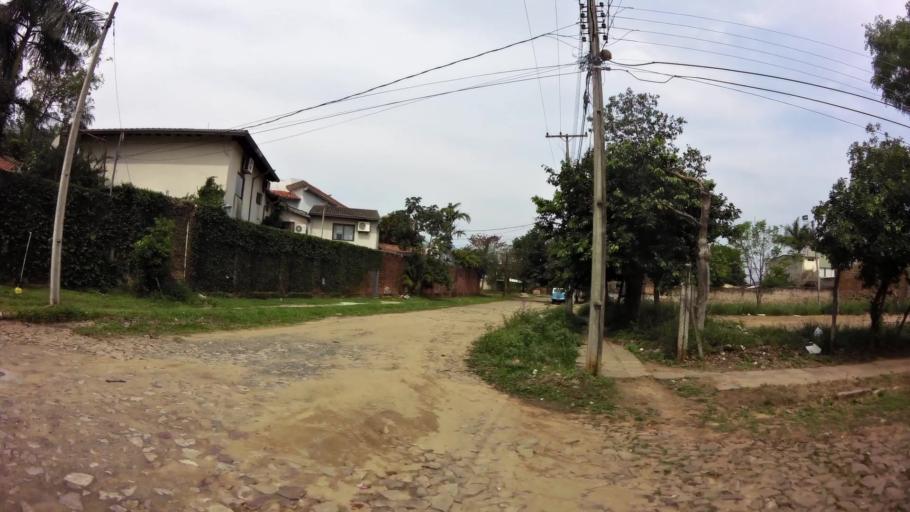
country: PY
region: Central
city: Fernando de la Mora
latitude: -25.2707
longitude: -57.5572
